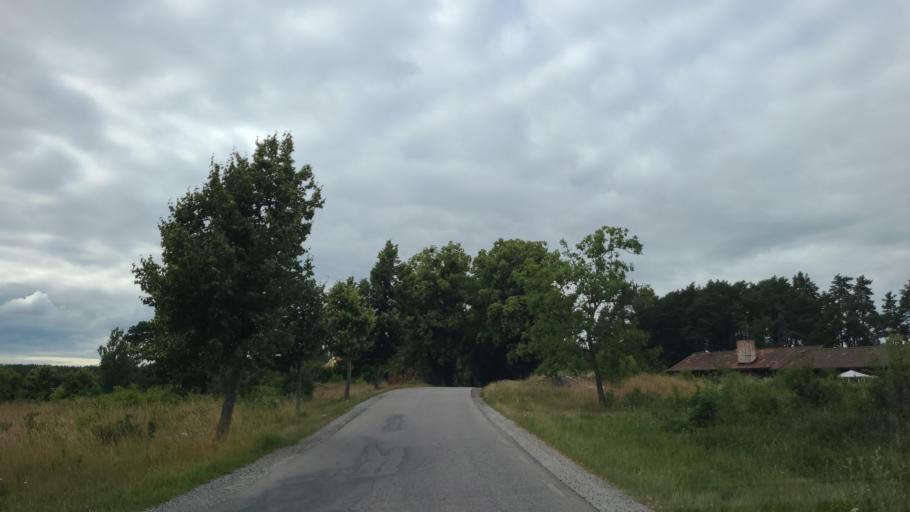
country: SE
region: Stockholm
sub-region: Upplands-Bro Kommun
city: Bro
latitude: 59.5059
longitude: 17.5731
